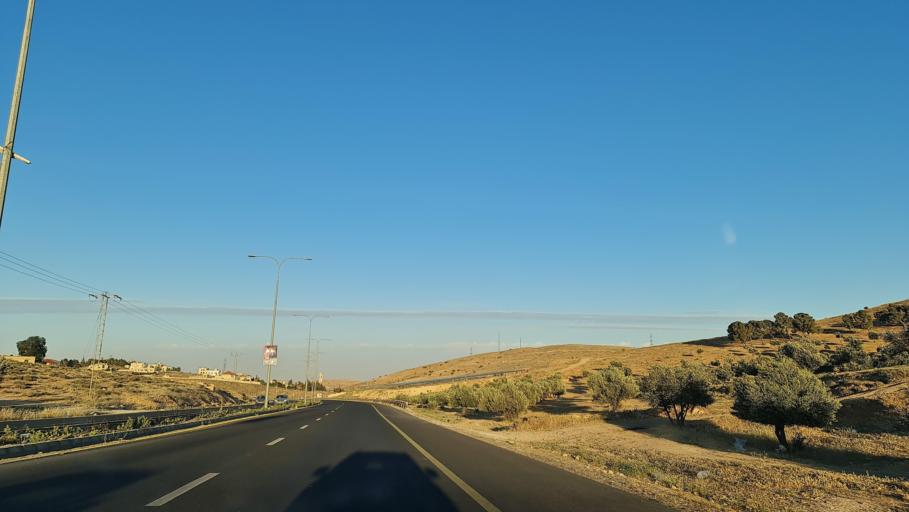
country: JO
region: Zarqa
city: Russeifa
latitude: 32.0912
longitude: 35.9797
